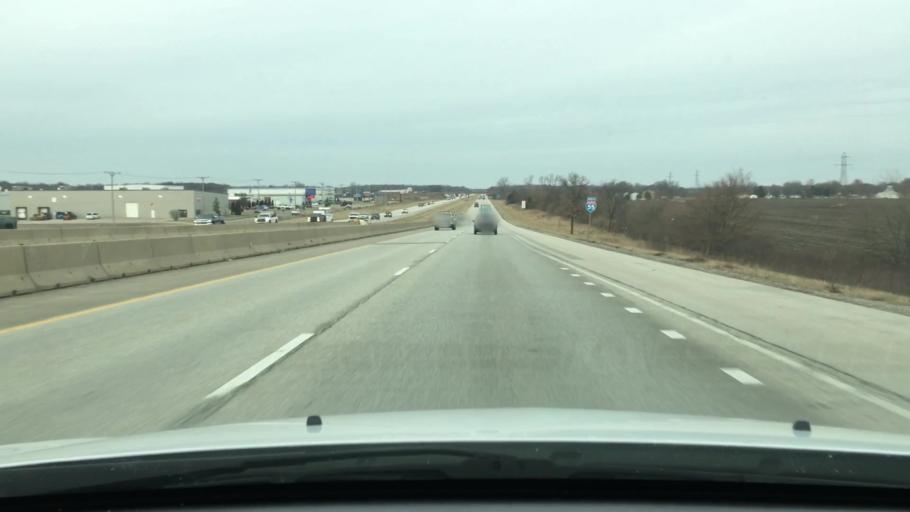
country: US
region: Illinois
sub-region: Sangamon County
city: Grandview
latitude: 39.8374
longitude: -89.5935
